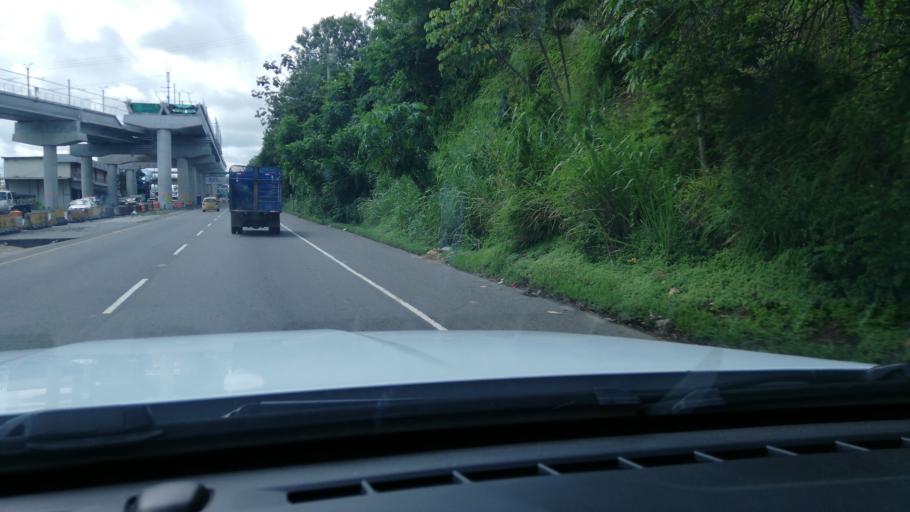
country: PA
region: Panama
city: Cabra Numero Uno
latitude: 9.1017
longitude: -79.3471
